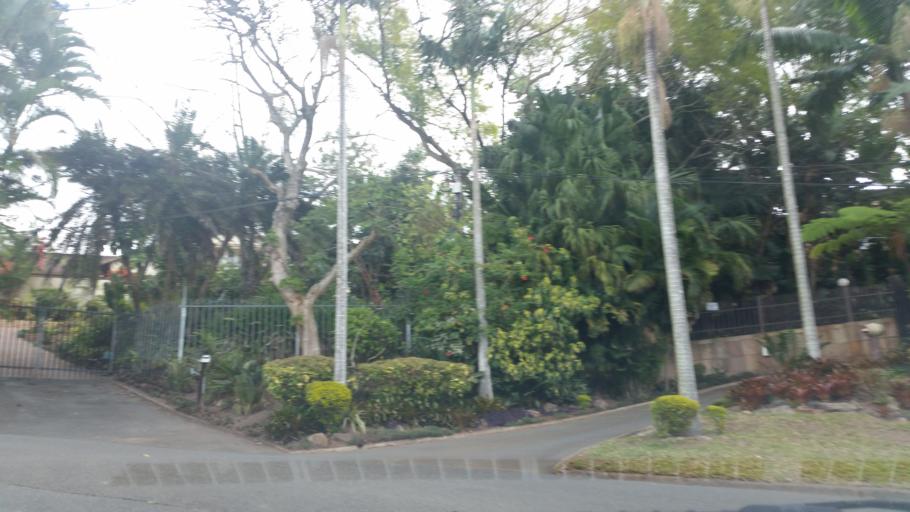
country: ZA
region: KwaZulu-Natal
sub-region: eThekwini Metropolitan Municipality
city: Berea
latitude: -29.8252
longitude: 30.9301
